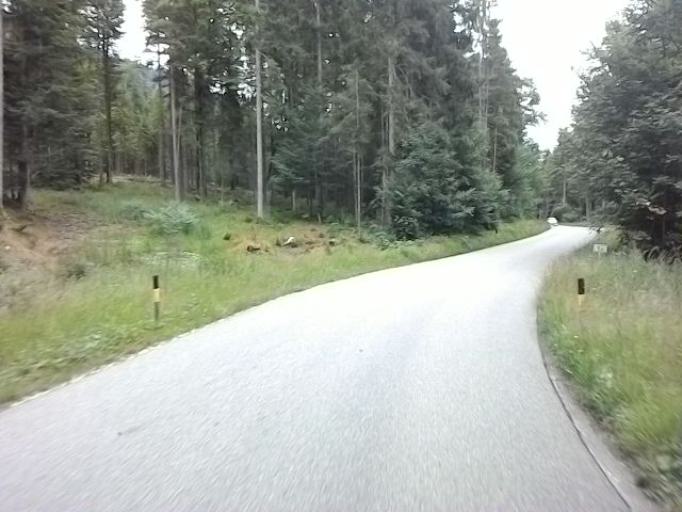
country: DE
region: Bavaria
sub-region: Upper Bavaria
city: Wallgau
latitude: 47.5358
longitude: 11.3298
